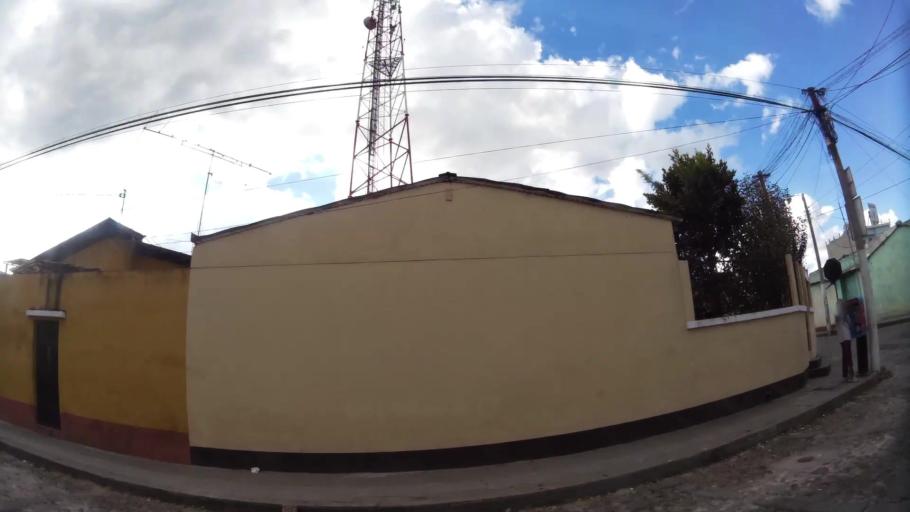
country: GT
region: Quetzaltenango
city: Quetzaltenango
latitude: 14.8412
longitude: -91.5290
